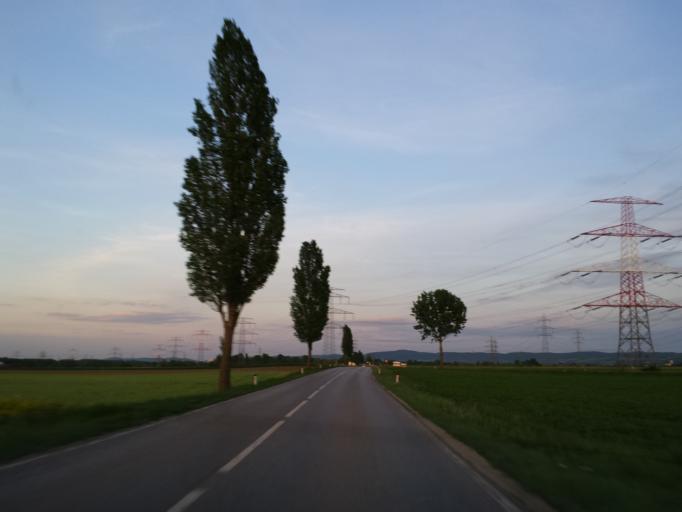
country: AT
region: Lower Austria
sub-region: Politischer Bezirk Tulln
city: Langenrohr
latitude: 48.3254
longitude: 15.9728
